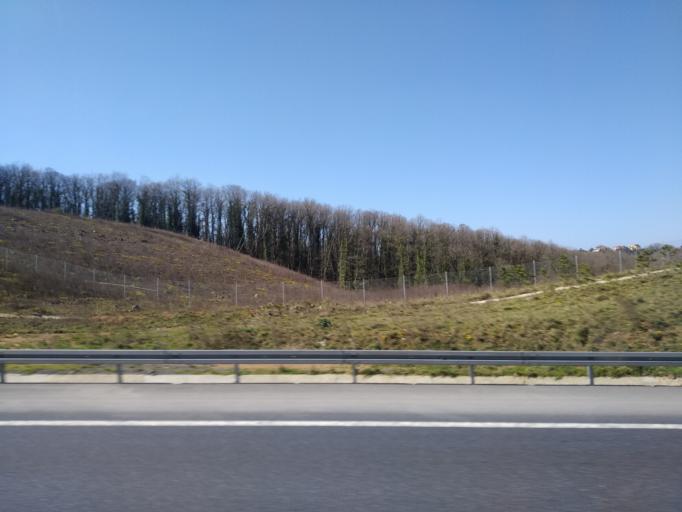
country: TR
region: Istanbul
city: Sancaktepe
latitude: 41.0752
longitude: 29.2781
